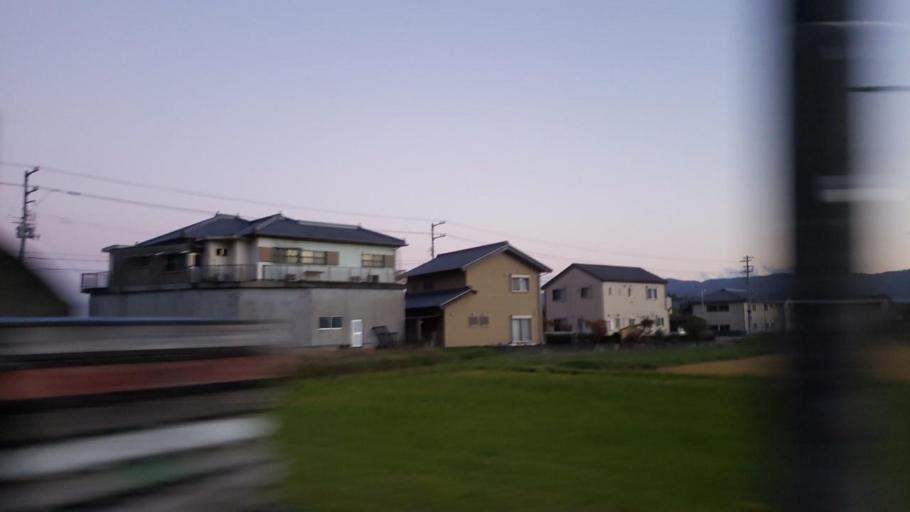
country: JP
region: Tokushima
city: Kamojimacho-jogejima
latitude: 34.1077
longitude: 134.3252
